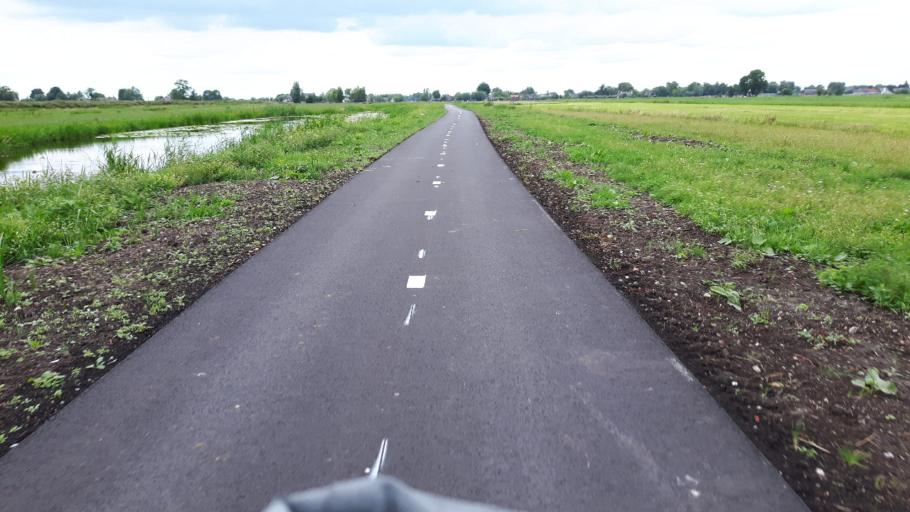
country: NL
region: South Holland
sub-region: Gemeente Vlist
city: Haastrecht
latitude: 51.9548
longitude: 4.7449
